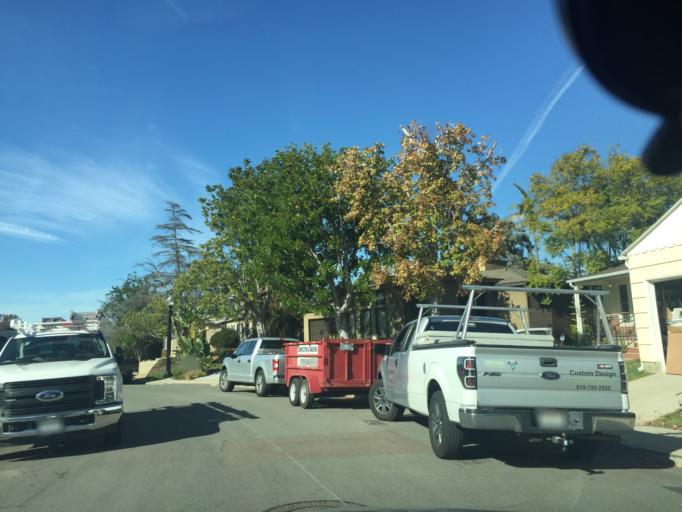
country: US
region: California
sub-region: San Diego County
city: Lemon Grove
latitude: 32.7630
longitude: -117.0910
